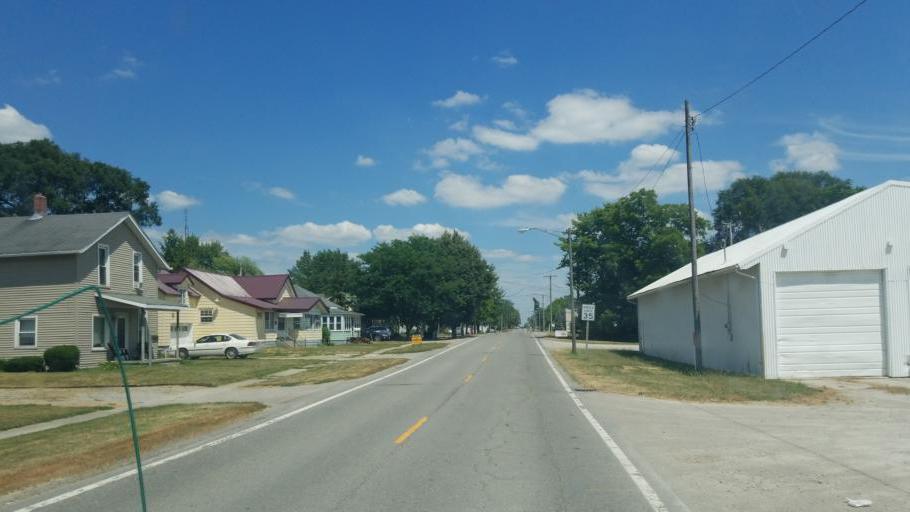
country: US
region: Ohio
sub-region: Defiance County
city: Hicksville
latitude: 41.2959
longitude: -84.7522
